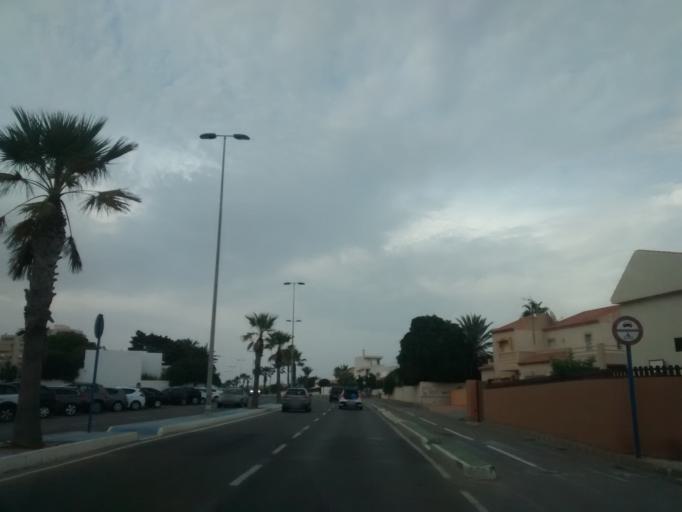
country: ES
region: Murcia
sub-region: Murcia
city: La Manga del Mar Menor
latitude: 37.7081
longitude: -0.7425
